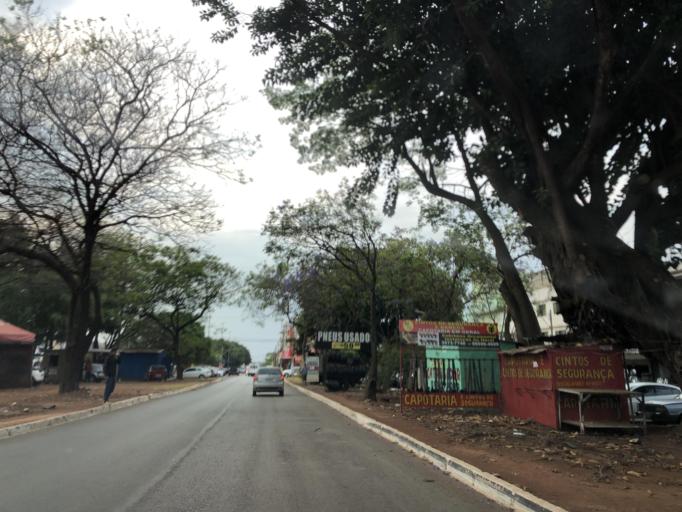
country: BR
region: Federal District
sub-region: Brasilia
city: Brasilia
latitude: -15.8049
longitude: -48.0856
